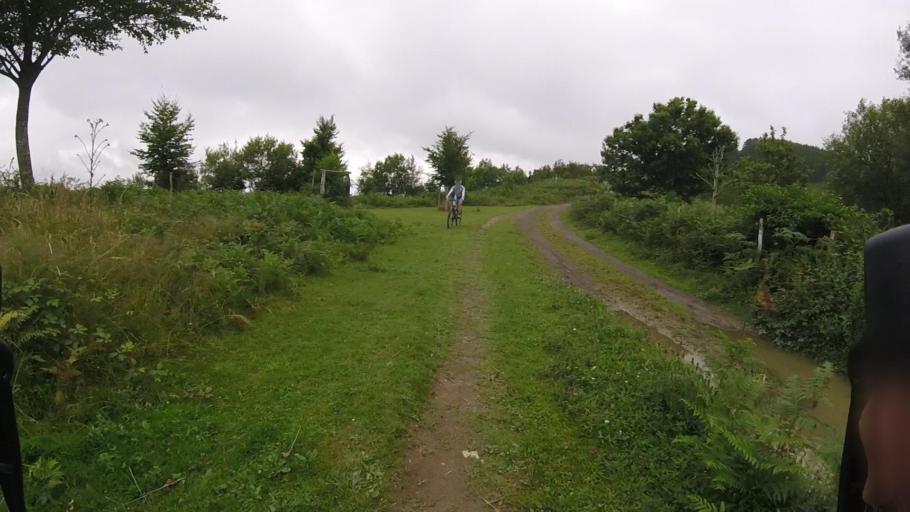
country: ES
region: Navarre
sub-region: Provincia de Navarra
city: Arano
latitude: 43.2524
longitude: -1.8888
